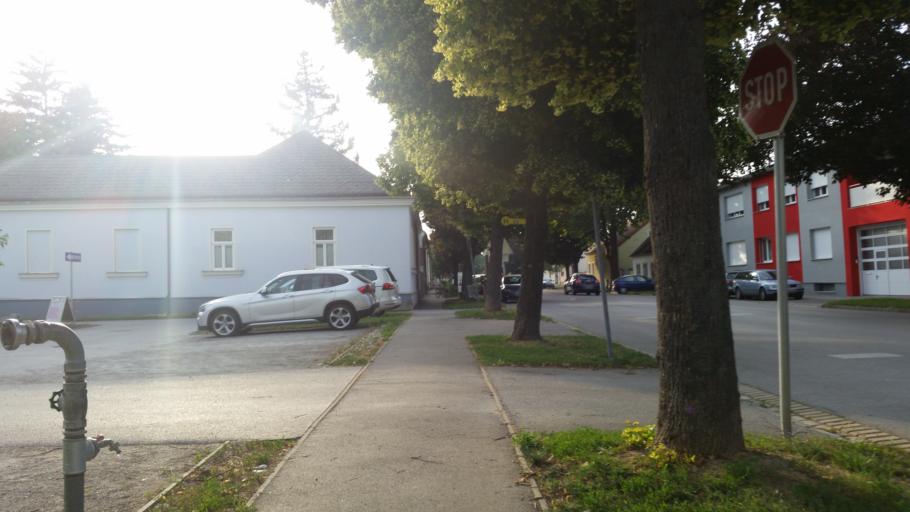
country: AT
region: Lower Austria
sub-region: Politischer Bezirk Mistelbach
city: Wolkersdorf im Weinviertel
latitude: 48.3841
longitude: 16.5210
